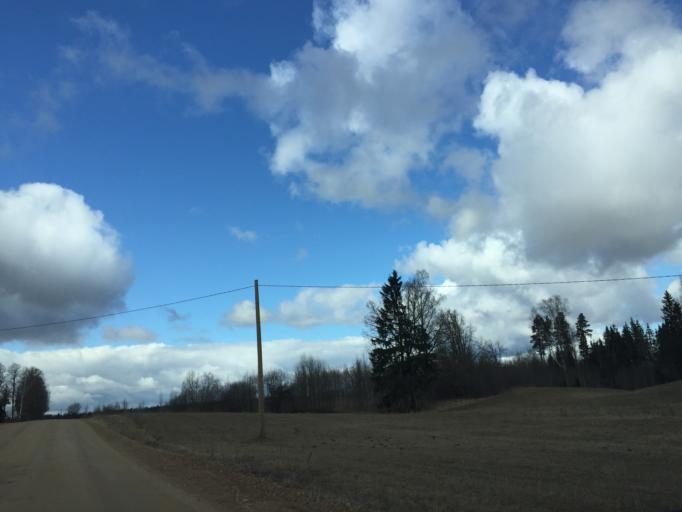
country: LV
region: Akniste
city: Akniste
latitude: 56.1121
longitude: 25.8703
